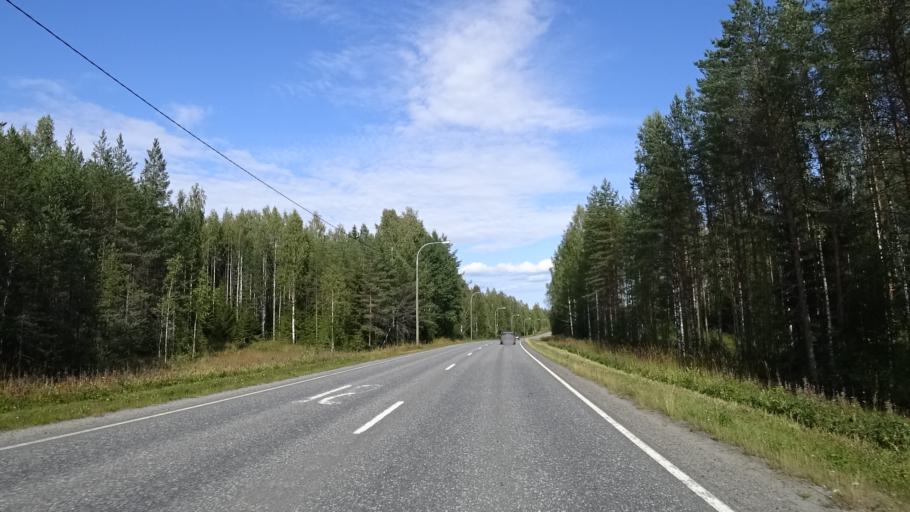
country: FI
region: North Karelia
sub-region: Joensuu
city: Eno
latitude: 62.7954
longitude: 30.0928
